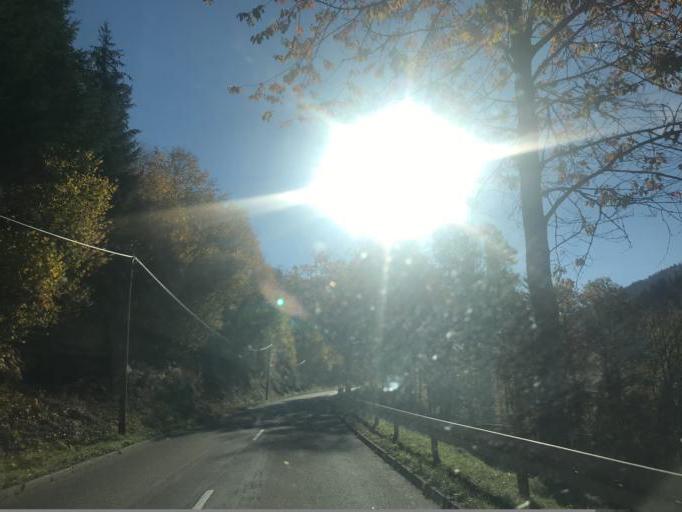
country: DE
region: Baden-Wuerttemberg
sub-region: Freiburg Region
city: Gutenbach
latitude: 48.0533
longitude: 8.1057
